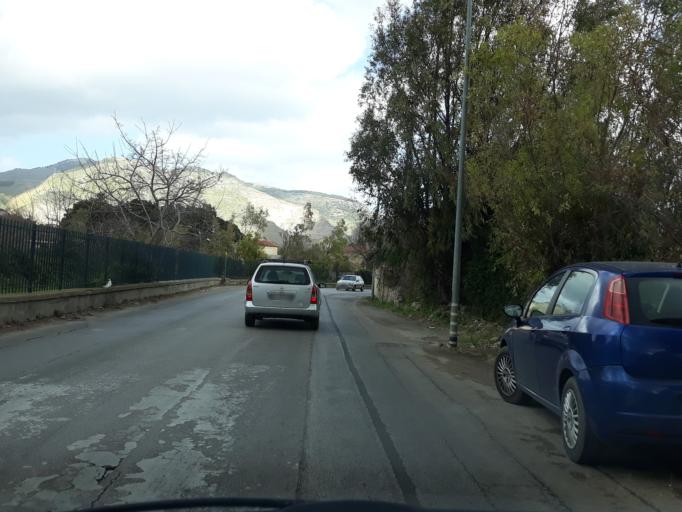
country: IT
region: Sicily
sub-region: Palermo
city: Piano dei Geli
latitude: 38.1151
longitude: 13.3036
